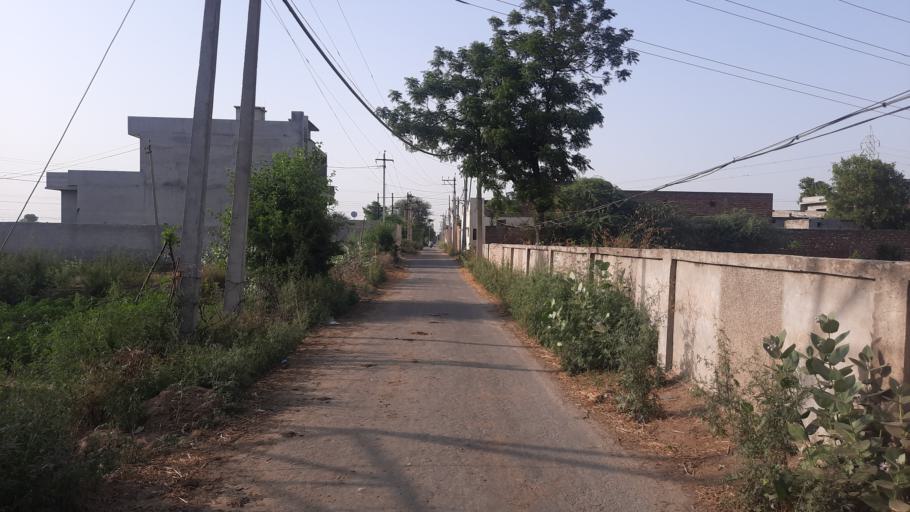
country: IN
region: Punjab
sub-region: Sangrur
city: Sunam
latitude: 30.1416
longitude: 75.8239
